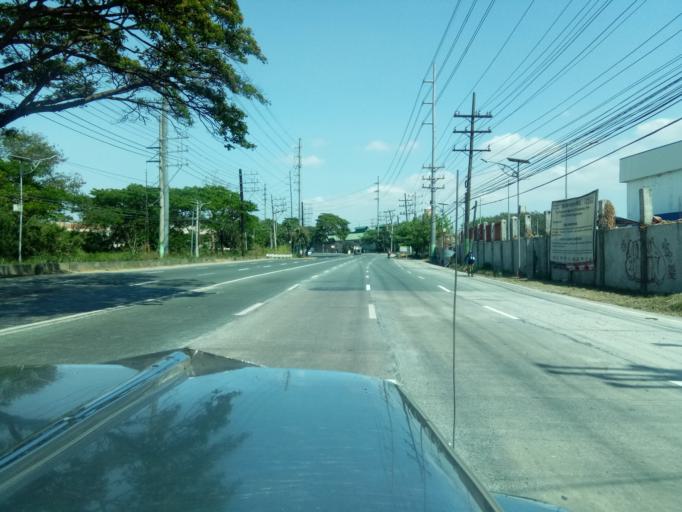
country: PH
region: Calabarzon
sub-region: Province of Cavite
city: Manggahan
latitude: 14.2918
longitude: 120.9249
